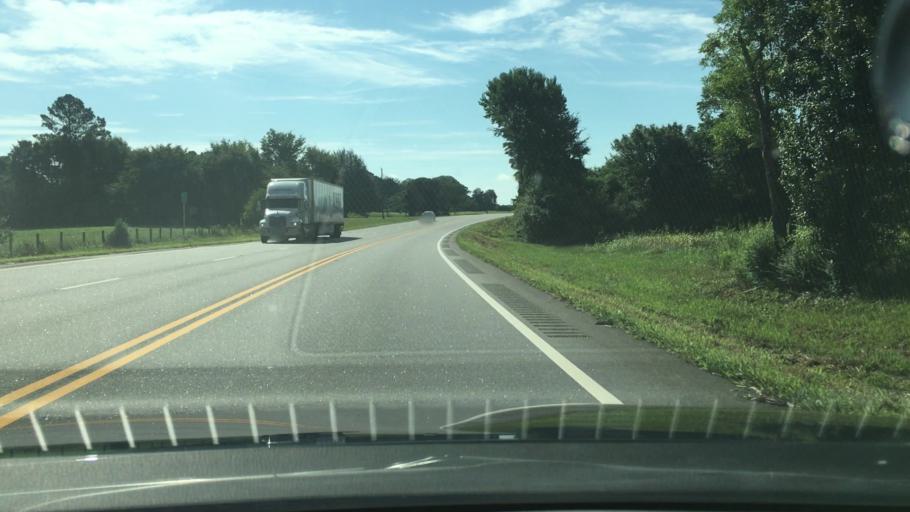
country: US
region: Georgia
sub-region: Putnam County
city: Jefferson
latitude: 33.4715
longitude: -83.4207
